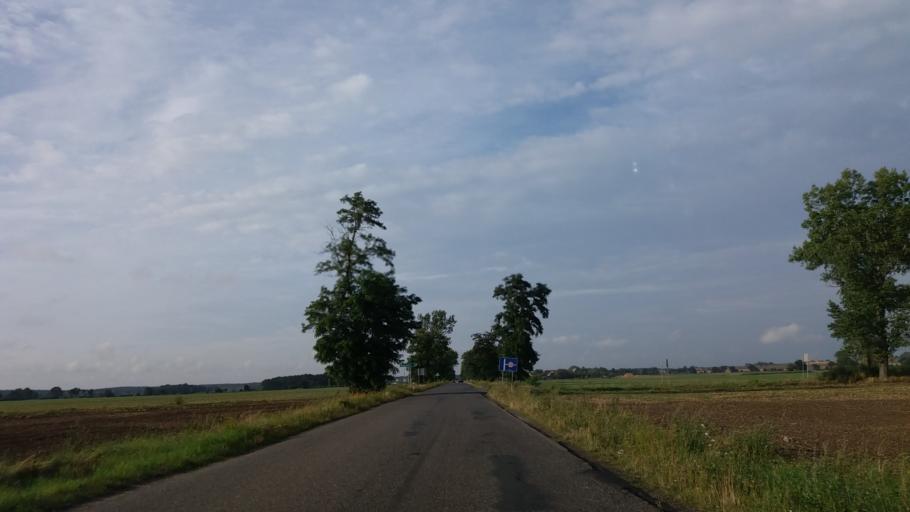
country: PL
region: Lower Silesian Voivodeship
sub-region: Powiat legnicki
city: Prochowice
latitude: 51.2037
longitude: 16.3468
